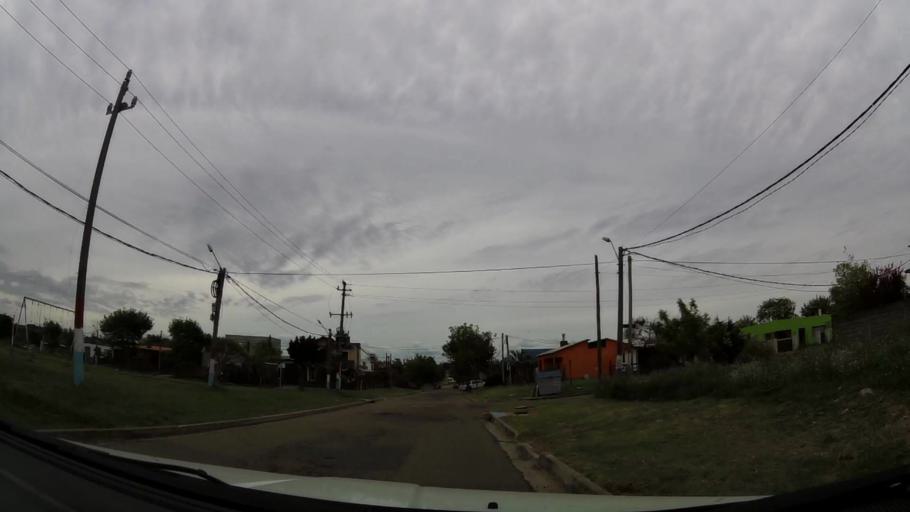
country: UY
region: Maldonado
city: Maldonado
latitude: -34.8911
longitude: -54.9500
